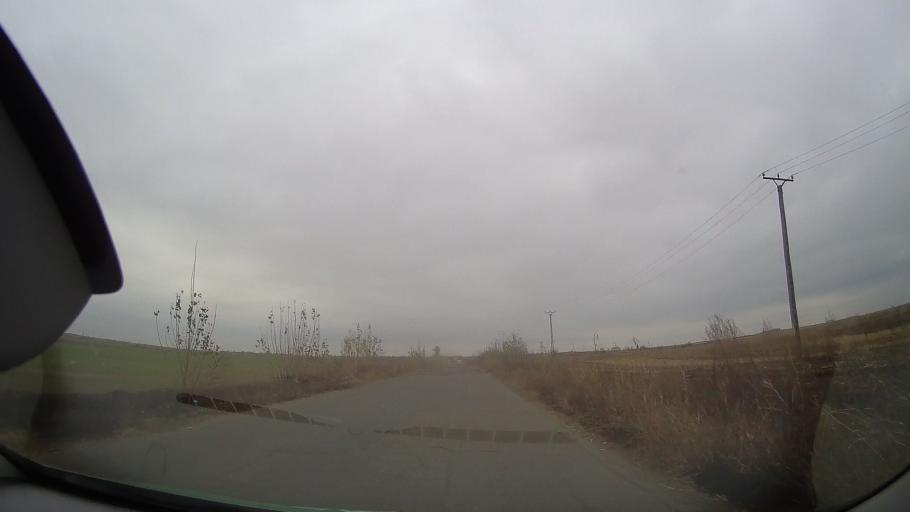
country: RO
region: Braila
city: Dudesti
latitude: 44.9262
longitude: 27.4281
